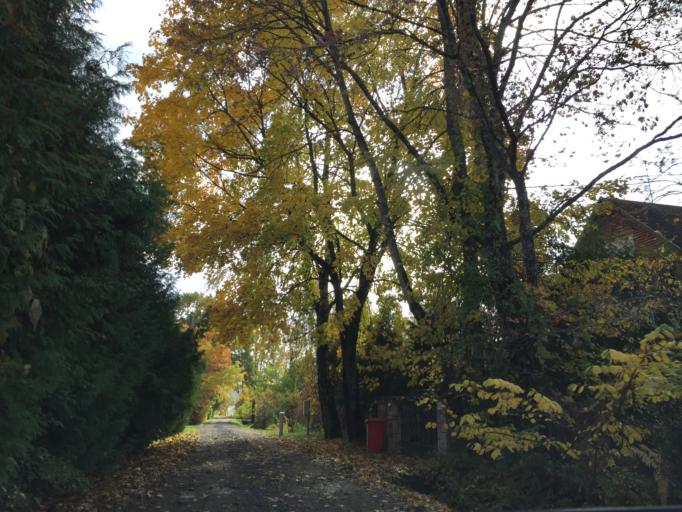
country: LV
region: Lielvarde
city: Lielvarde
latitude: 56.7177
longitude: 24.7973
